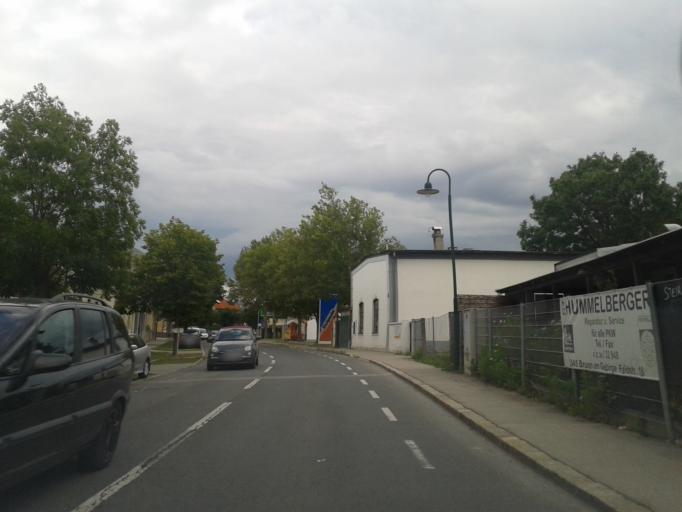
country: AT
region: Lower Austria
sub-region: Politischer Bezirk Modling
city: Perchtoldsdorf
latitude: 48.1166
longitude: 16.2705
